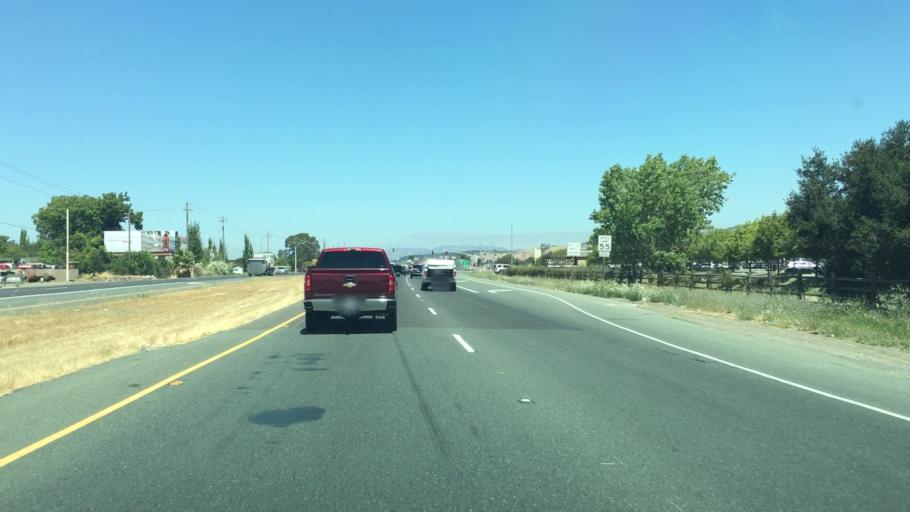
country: US
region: California
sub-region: Napa County
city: American Canyon
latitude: 38.1817
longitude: -122.2550
